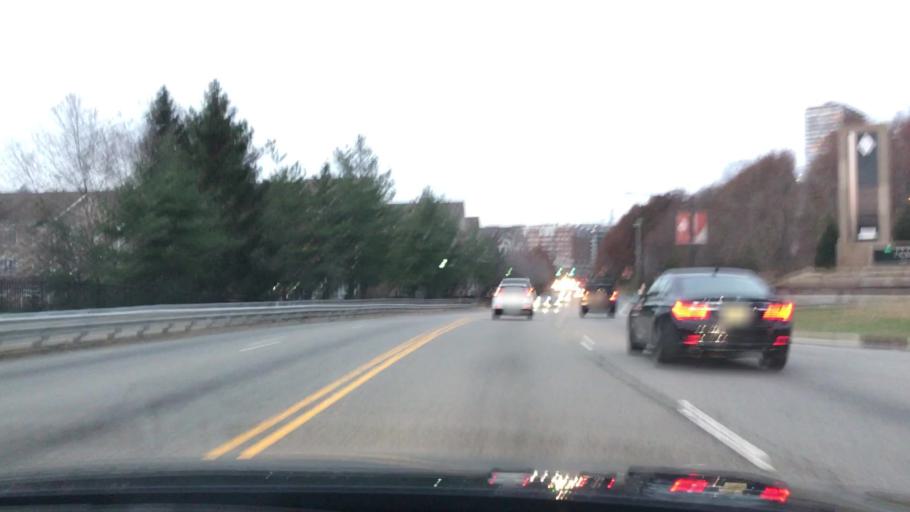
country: US
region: New Jersey
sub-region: Hudson County
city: Guttenberg
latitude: 40.7885
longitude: -74.0007
